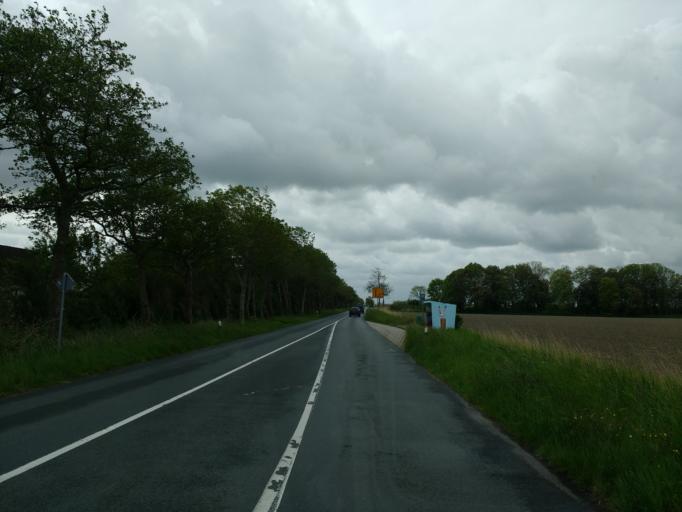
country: DE
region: Lower Saxony
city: Schillig
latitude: 53.6955
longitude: 8.0133
